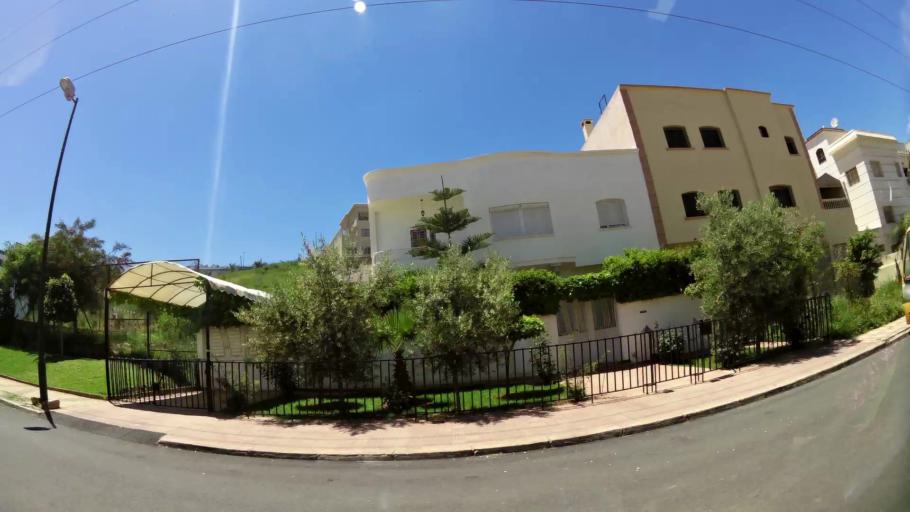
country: MA
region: Meknes-Tafilalet
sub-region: Meknes
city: Meknes
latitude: 33.9064
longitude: -5.5500
